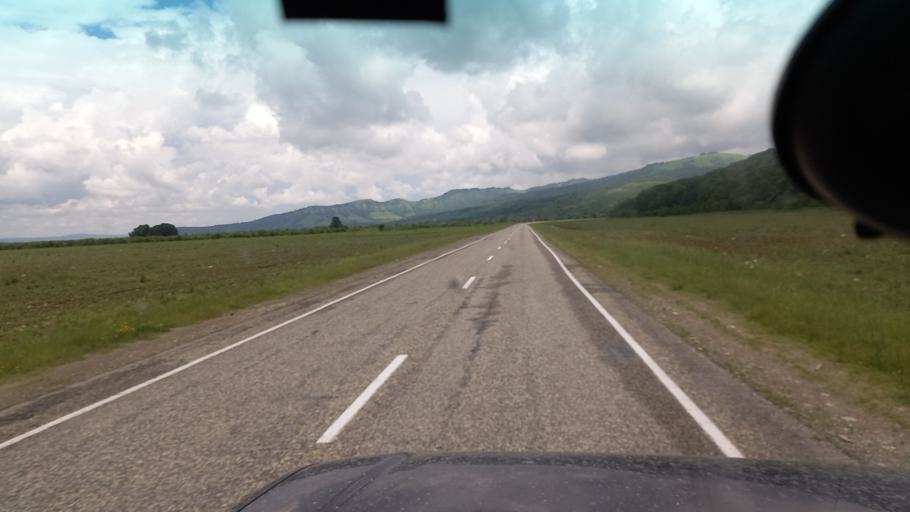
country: RU
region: Krasnodarskiy
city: Psebay
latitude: 44.1006
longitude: 40.8182
